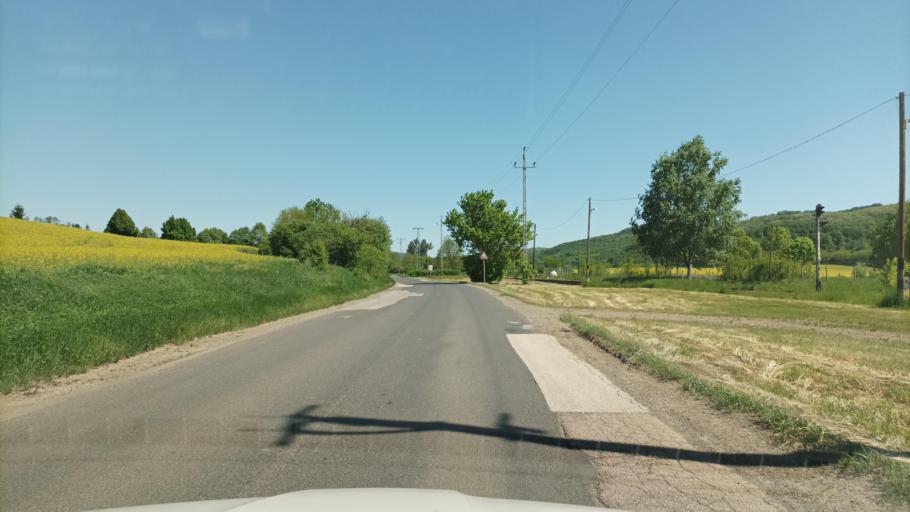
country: HU
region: Pest
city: Acsa
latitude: 47.8054
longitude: 19.3868
